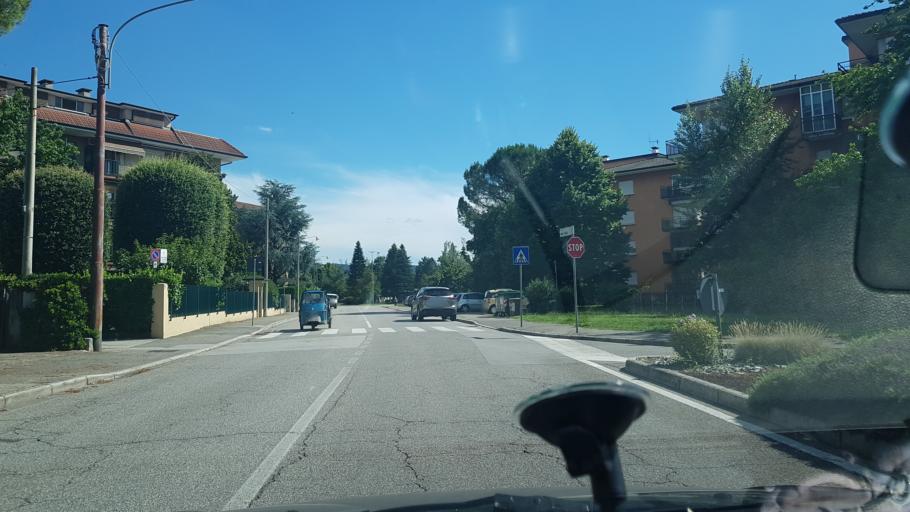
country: IT
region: Friuli Venezia Giulia
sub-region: Provincia di Gorizia
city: Gorizia
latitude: 45.9320
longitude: 13.6218
